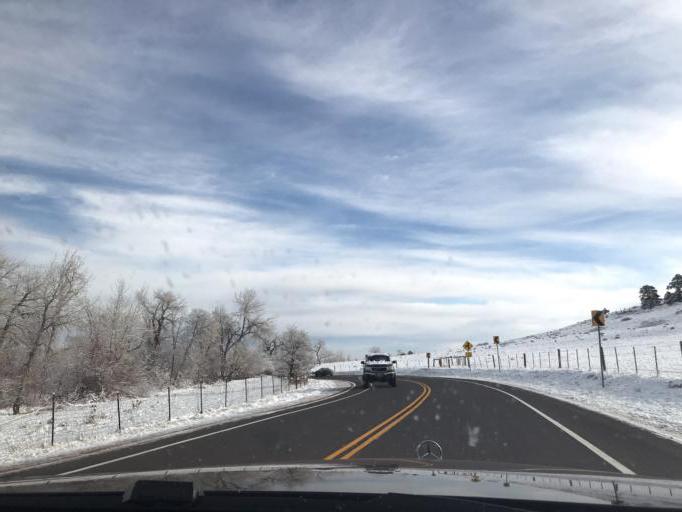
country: US
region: Colorado
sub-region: Boulder County
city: Superior
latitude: 39.9624
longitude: -105.2137
